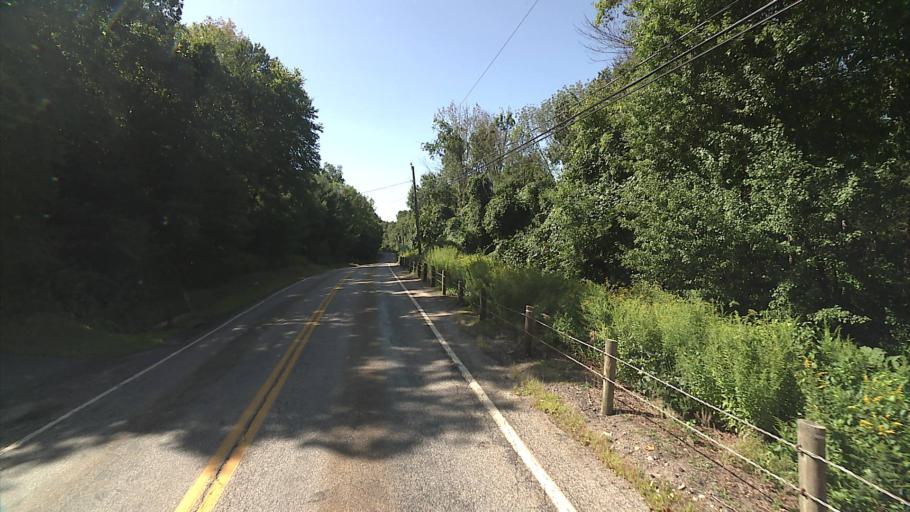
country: US
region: Connecticut
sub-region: Litchfield County
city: Plymouth
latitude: 41.6995
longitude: -73.0561
